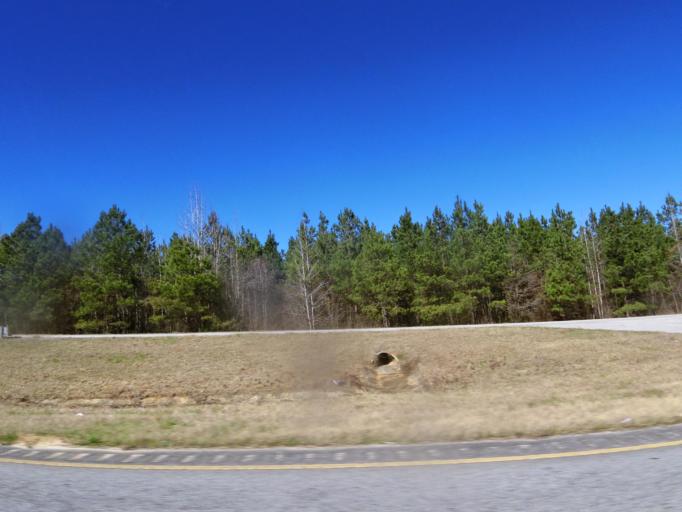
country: US
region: Alabama
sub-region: Bullock County
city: Union Springs
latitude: 32.1460
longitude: -85.6348
